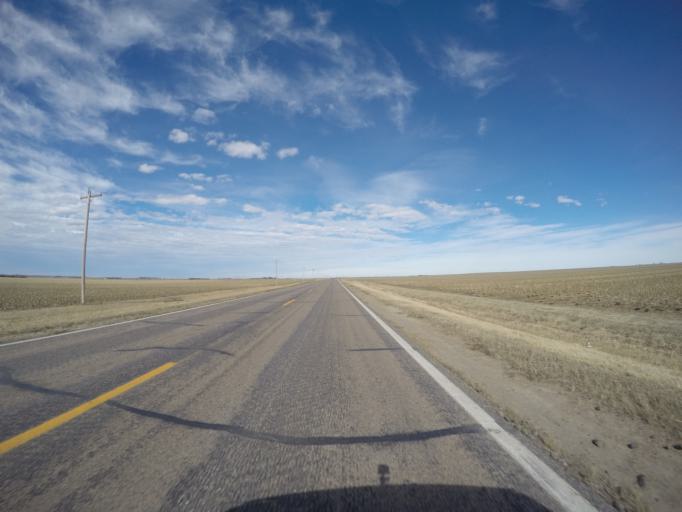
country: US
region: Nebraska
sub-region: Franklin County
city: Franklin
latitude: 40.2279
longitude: -98.9524
